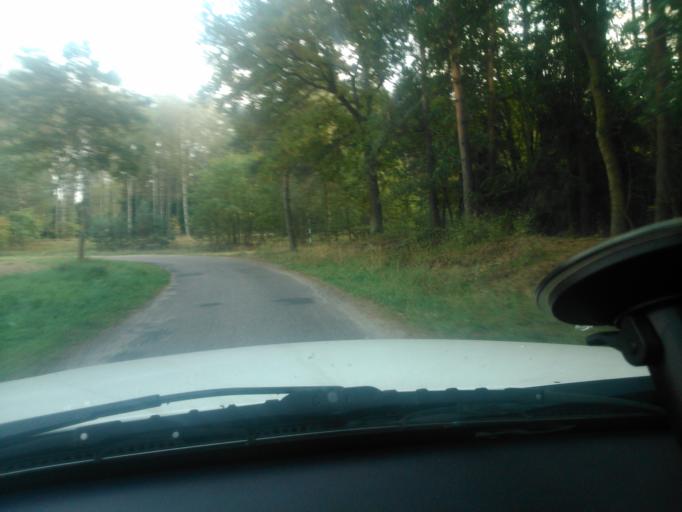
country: PL
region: Kujawsko-Pomorskie
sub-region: Powiat wabrzeski
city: Debowa Laka
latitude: 53.1888
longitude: 19.1179
